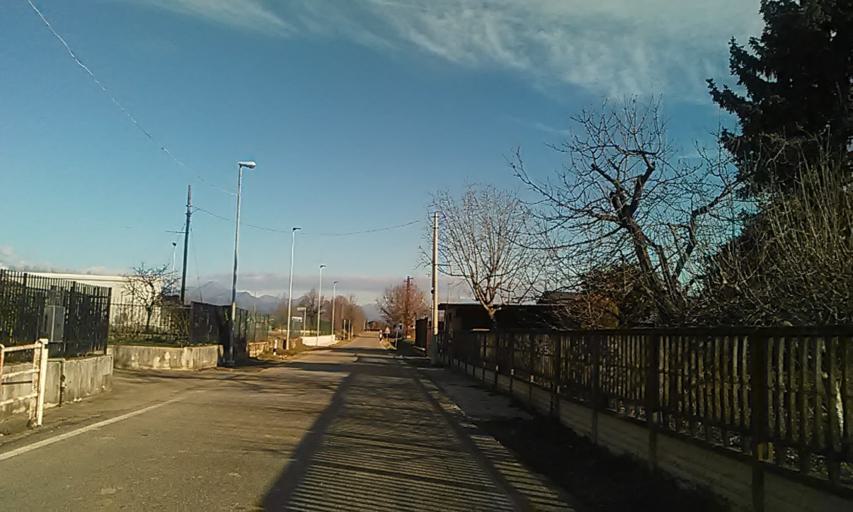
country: IT
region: Piedmont
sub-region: Provincia di Vercelli
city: Buronzo
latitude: 45.4833
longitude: 8.2723
